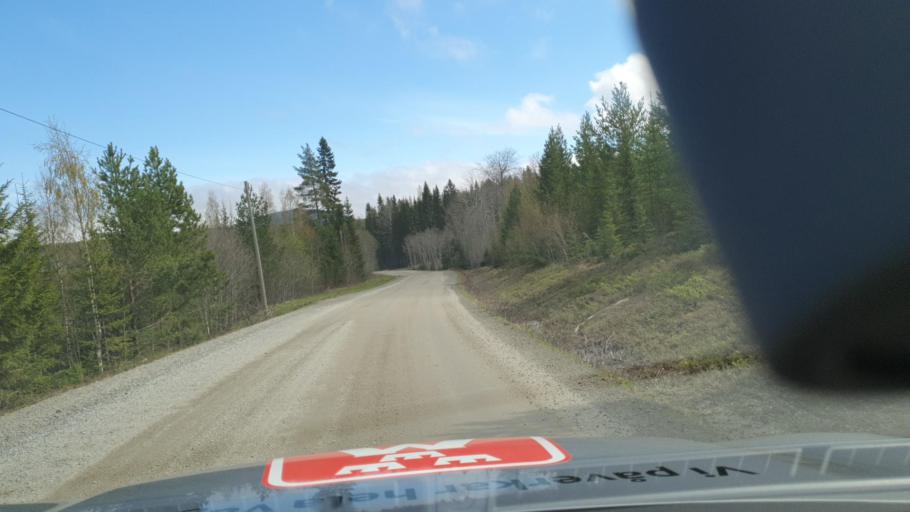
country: SE
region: Vaesterbotten
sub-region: Bjurholms Kommun
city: Bjurholm
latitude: 63.7017
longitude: 18.9248
